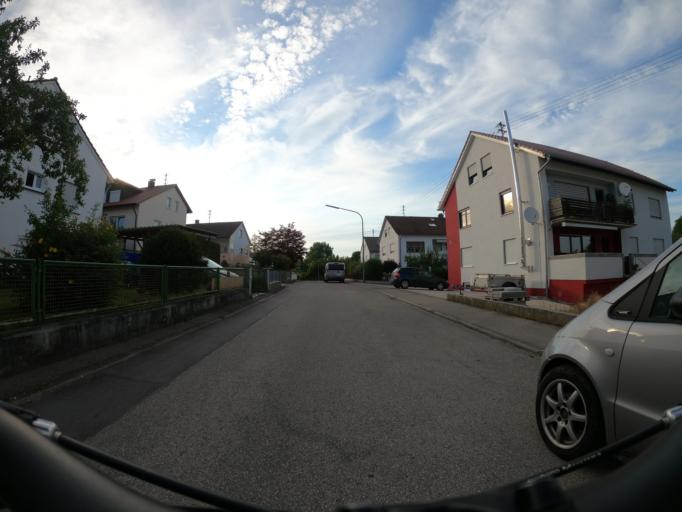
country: DE
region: Bavaria
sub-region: Swabia
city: Nersingen
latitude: 48.4314
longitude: 10.1650
